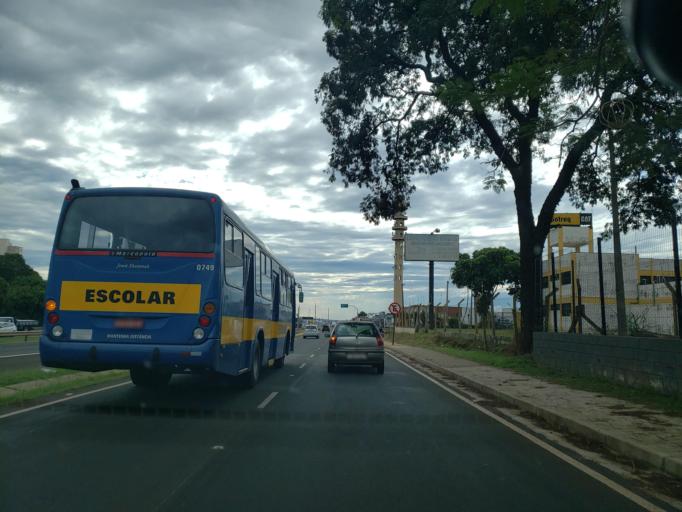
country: BR
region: Sao Paulo
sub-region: Bauru
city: Bauru
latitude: -22.3354
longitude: -49.0487
